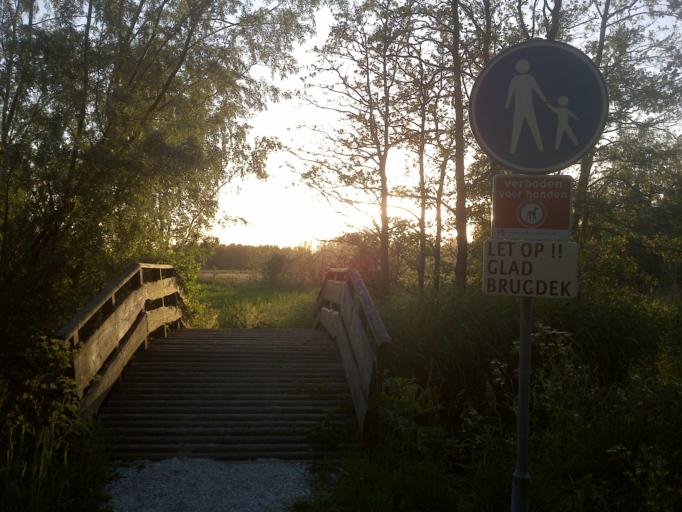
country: NL
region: South Holland
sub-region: Gemeente Leiden
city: Leiden
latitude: 52.1394
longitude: 4.5044
